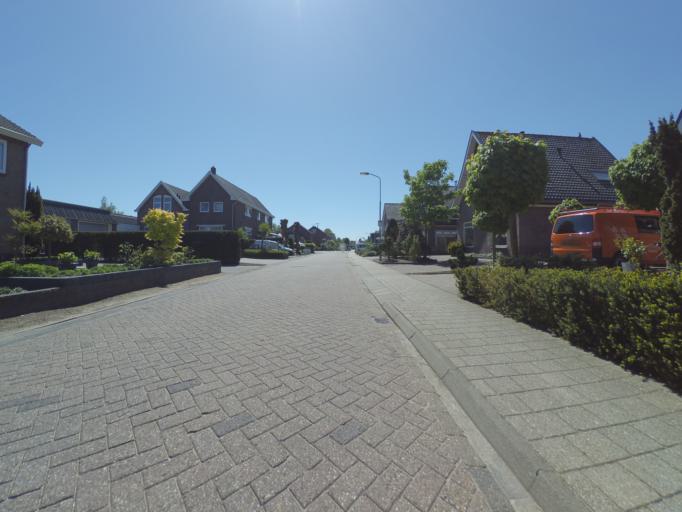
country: NL
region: Gelderland
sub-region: Gemeente Voorst
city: Twello
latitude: 52.2139
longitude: 6.1165
